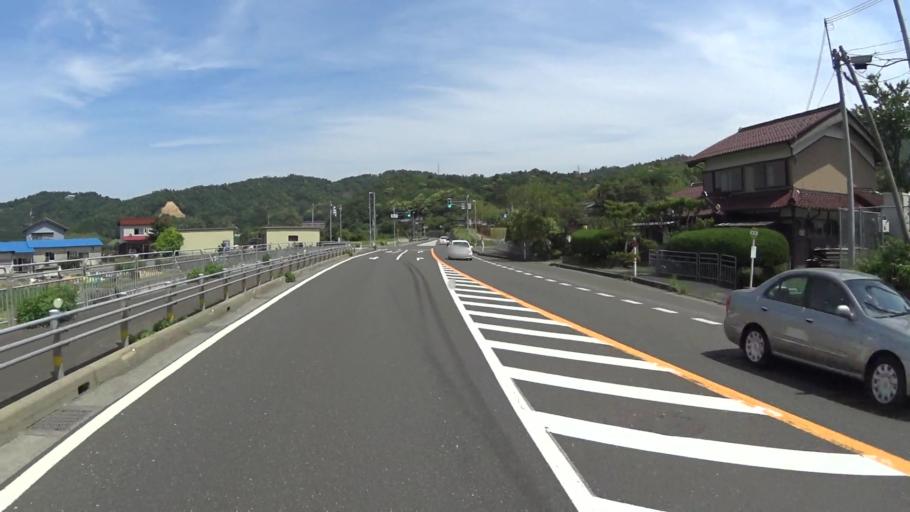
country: JP
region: Fukui
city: Obama
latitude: 35.4834
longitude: 135.7088
